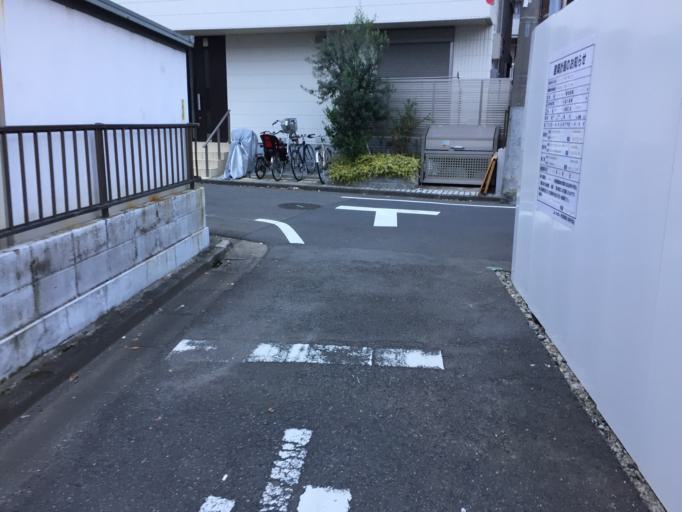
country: JP
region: Tokyo
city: Tokyo
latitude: 35.6423
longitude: 139.6646
